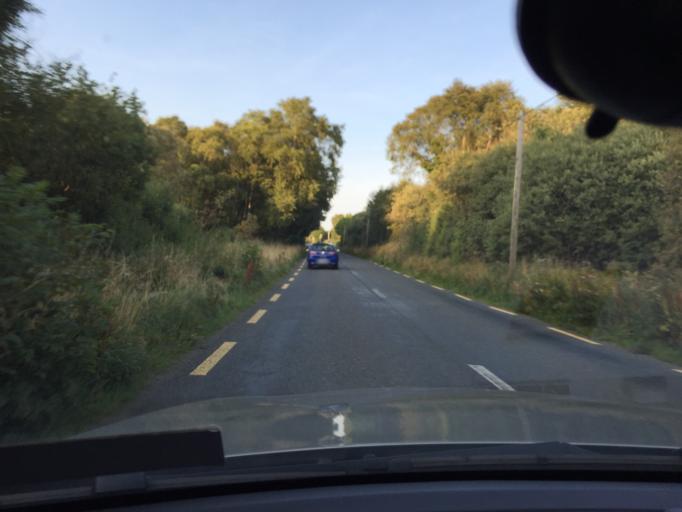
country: IE
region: Leinster
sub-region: Wicklow
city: Rathdrum
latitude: 53.0472
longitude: -6.2430
